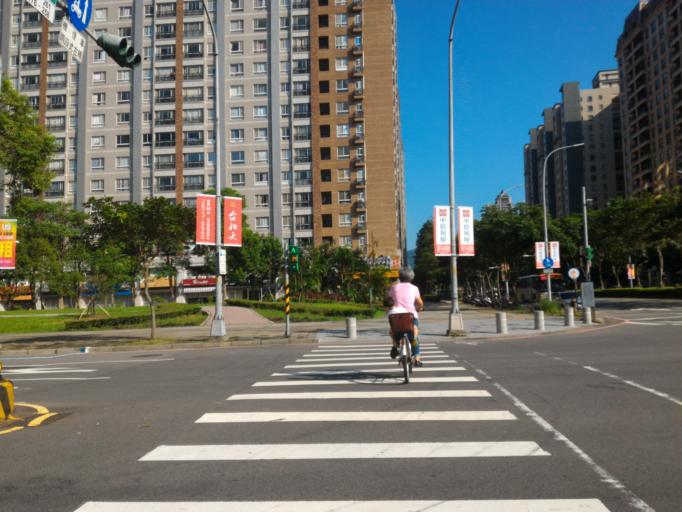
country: TW
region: Taiwan
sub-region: Taoyuan
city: Taoyuan
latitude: 24.9446
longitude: 121.3783
